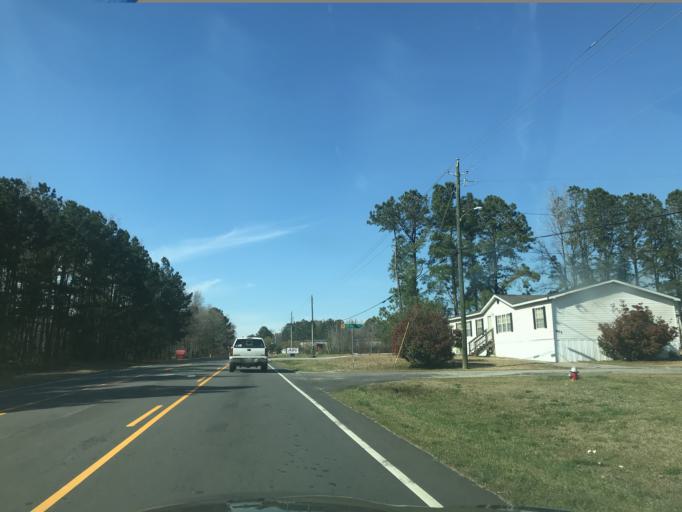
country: US
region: North Carolina
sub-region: Wake County
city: Fuquay-Varina
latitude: 35.5906
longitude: -78.7577
